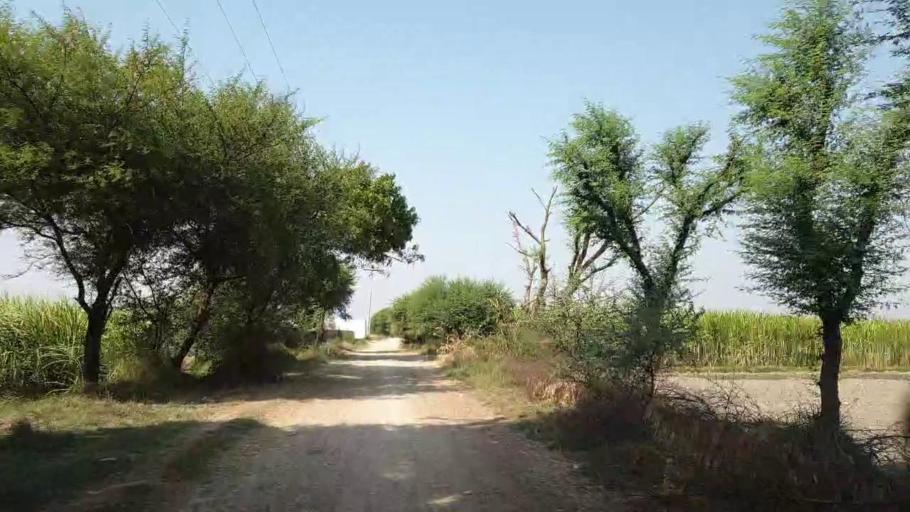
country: PK
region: Sindh
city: Tando Muhammad Khan
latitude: 25.0226
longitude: 68.4119
